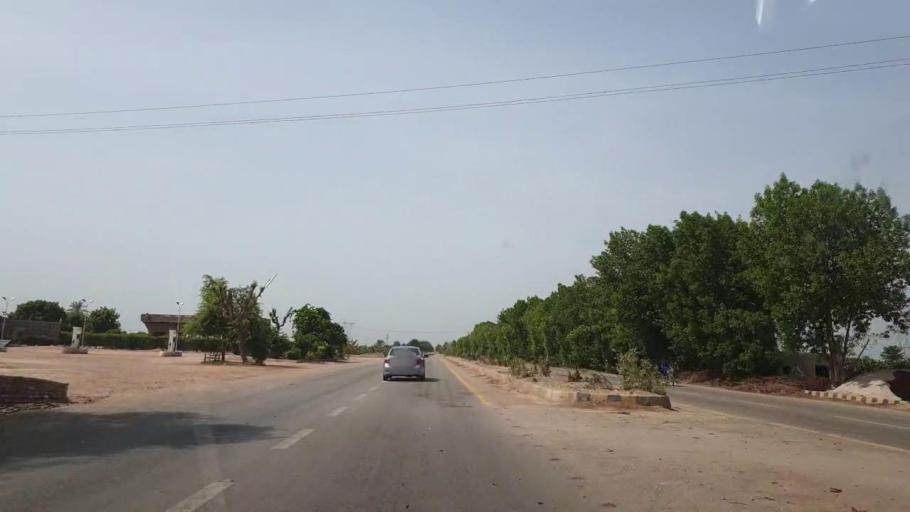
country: PK
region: Sindh
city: Sakrand
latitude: 26.1840
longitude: 68.2911
